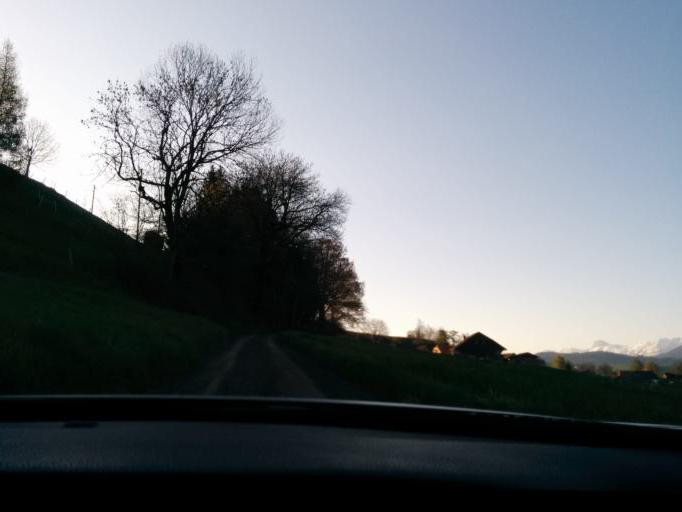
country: CH
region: Bern
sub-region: Bern-Mittelland District
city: Wahlern
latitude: 46.8389
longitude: 7.3961
